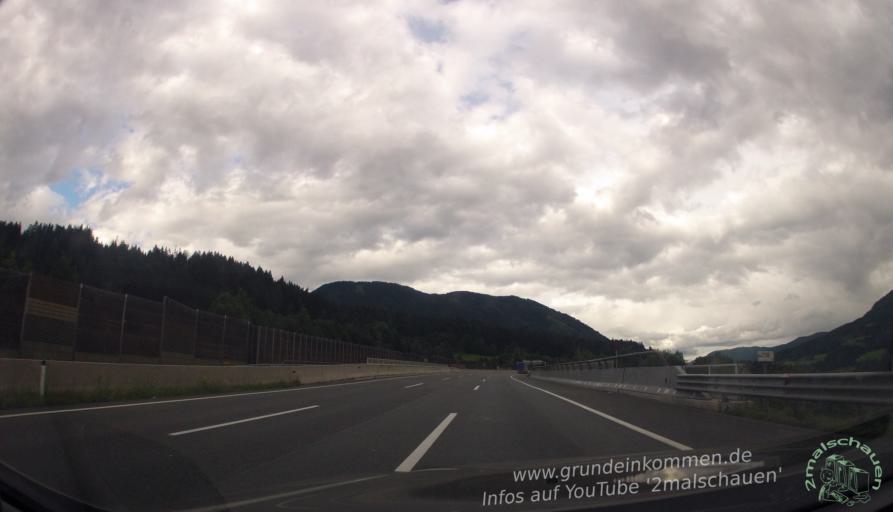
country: AT
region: Salzburg
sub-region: Politischer Bezirk Sankt Johann im Pongau
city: Bischofshofen
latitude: 47.4380
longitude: 13.2347
